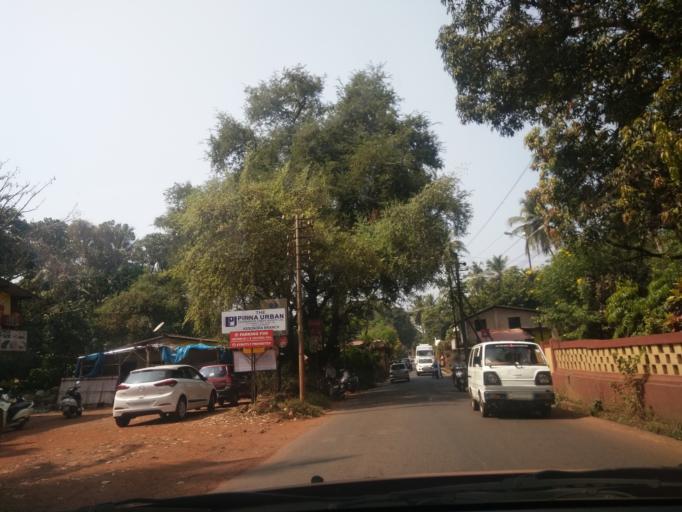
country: IN
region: Goa
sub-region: North Goa
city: Aldona
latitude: 15.6194
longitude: 73.8992
